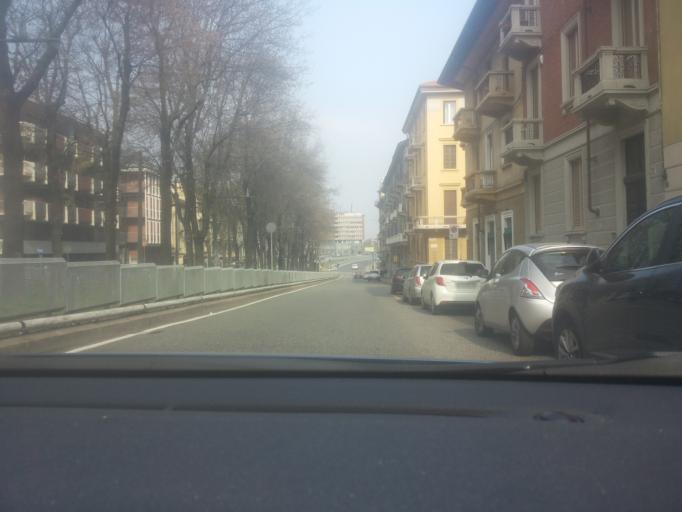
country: IT
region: Piedmont
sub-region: Provincia di Torino
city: Turin
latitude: 45.0660
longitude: 7.7103
